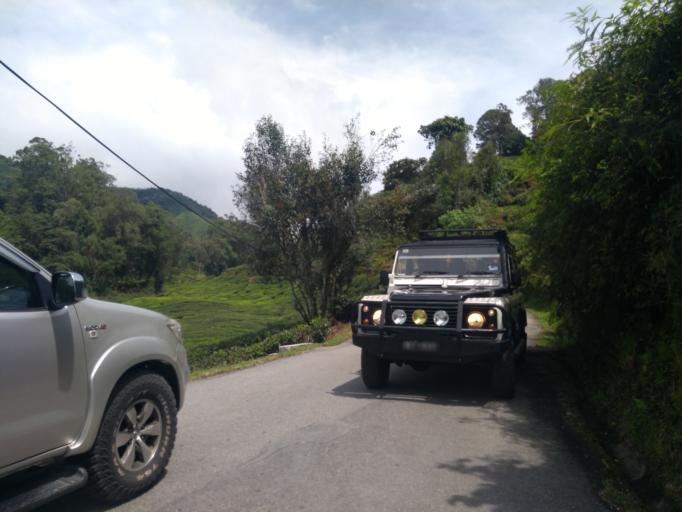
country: MY
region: Pahang
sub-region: Cameron Highlands
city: Tanah Rata
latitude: 4.5185
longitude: 101.4095
